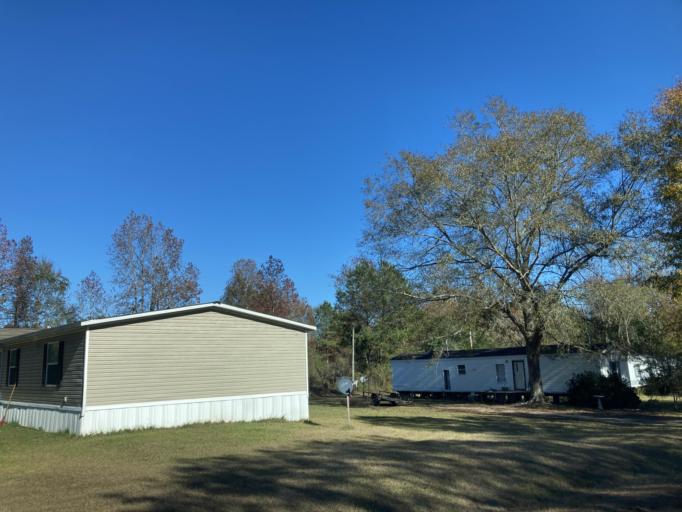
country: US
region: Mississippi
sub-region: Lamar County
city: Sumrall
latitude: 31.2985
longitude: -89.6414
